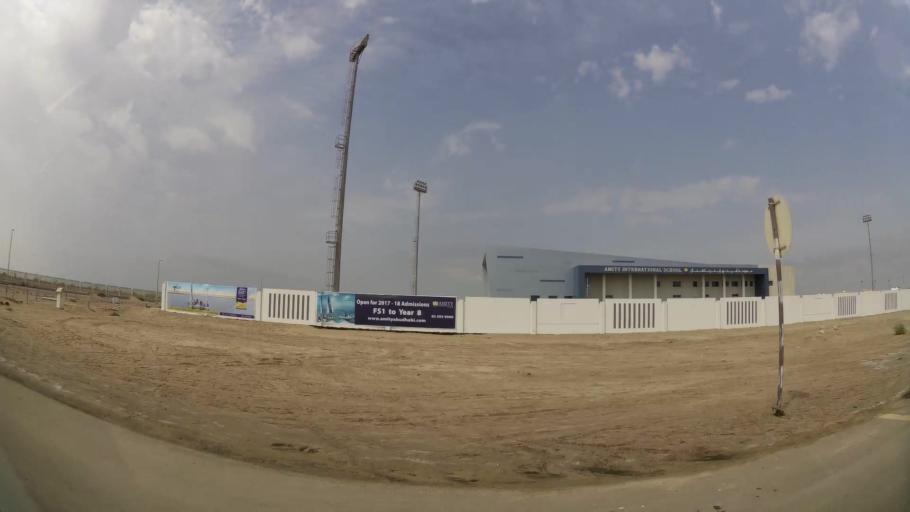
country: AE
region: Abu Dhabi
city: Abu Dhabi
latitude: 24.5361
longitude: 54.6333
